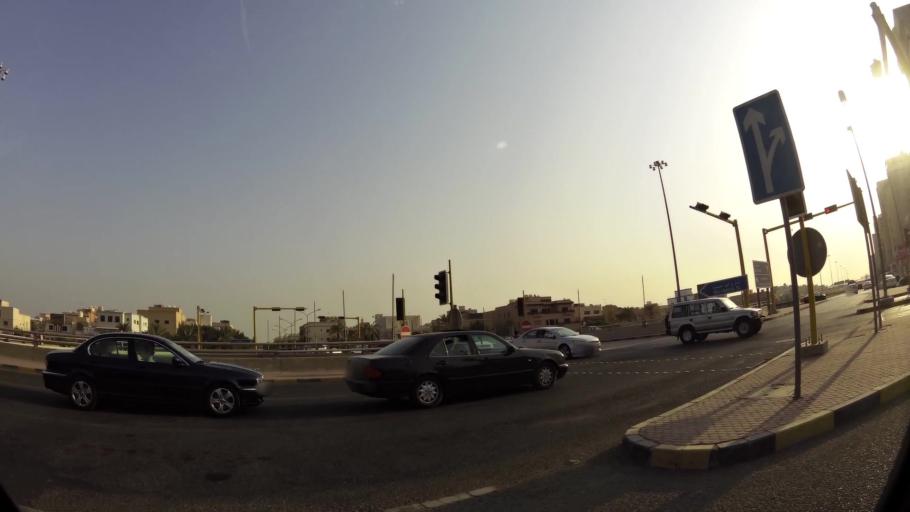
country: KW
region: Muhafazat Hawalli
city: As Salimiyah
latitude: 29.3237
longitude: 48.0660
